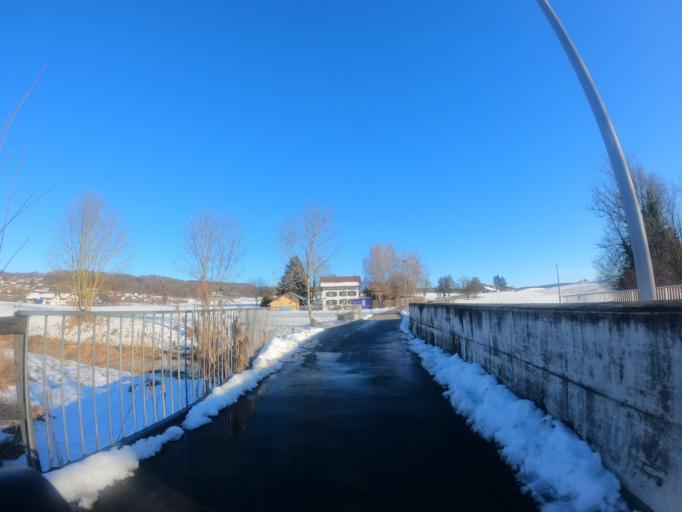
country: CH
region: Zurich
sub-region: Bezirk Affoltern
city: Affoltern / Unterdorf
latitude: 47.2869
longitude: 8.4401
